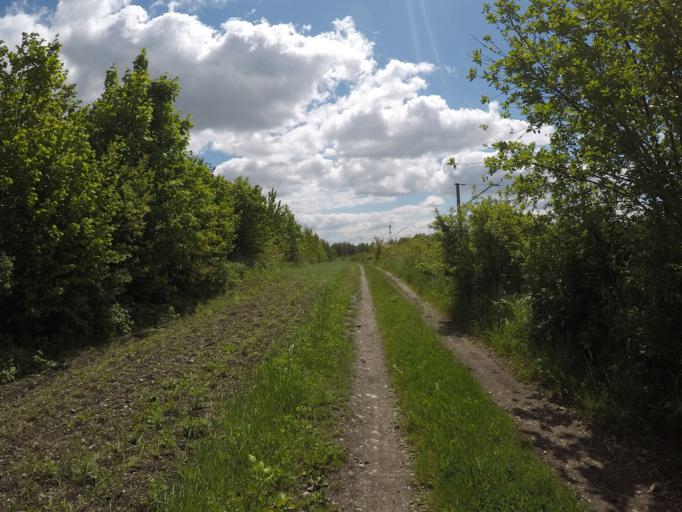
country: PL
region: Swietokrzyskie
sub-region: Powiat kielecki
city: Kostomloty Pierwsze
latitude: 50.9308
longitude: 20.6026
